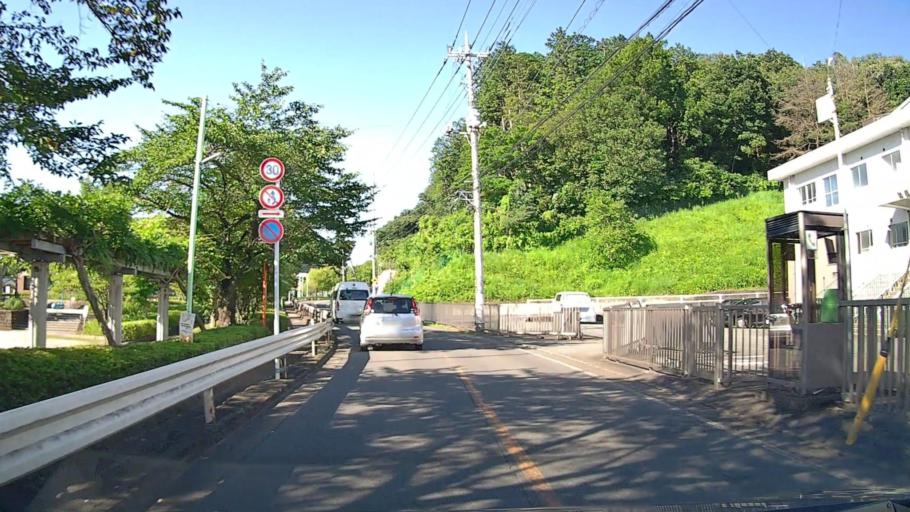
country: JP
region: Tokyo
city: Fussa
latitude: 35.7726
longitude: 139.3563
